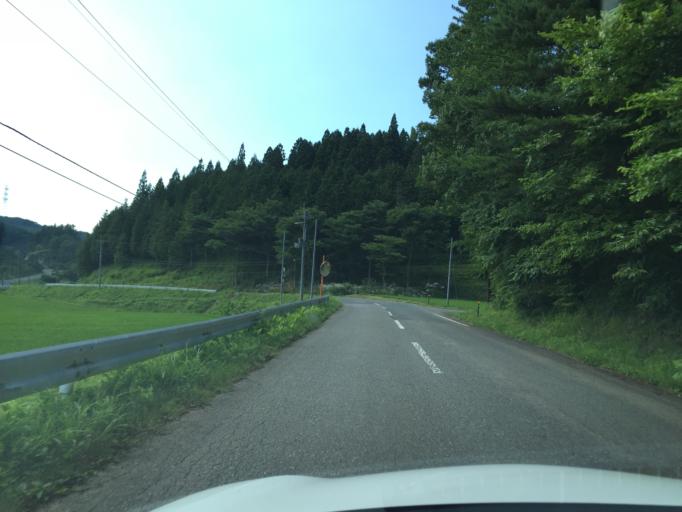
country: JP
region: Fukushima
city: Ishikawa
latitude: 37.1664
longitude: 140.6254
